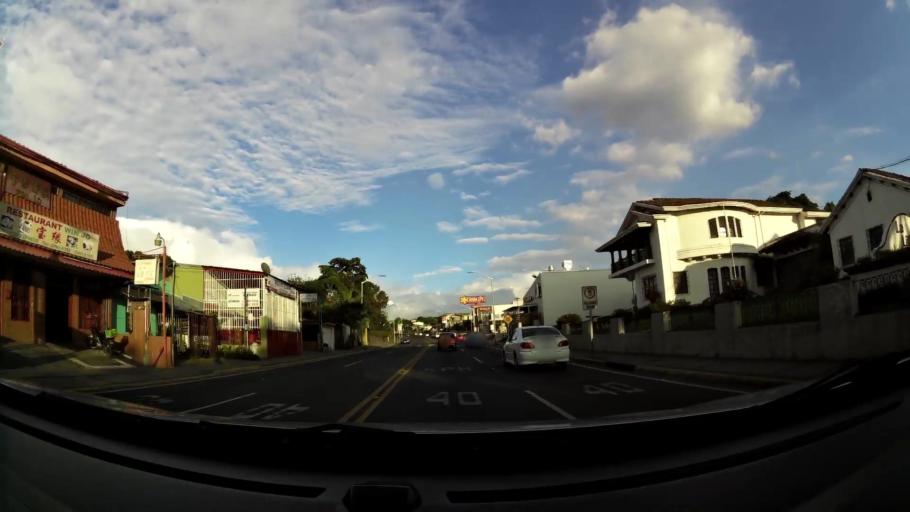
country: CR
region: Heredia
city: San Francisco
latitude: 9.9961
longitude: -84.1277
